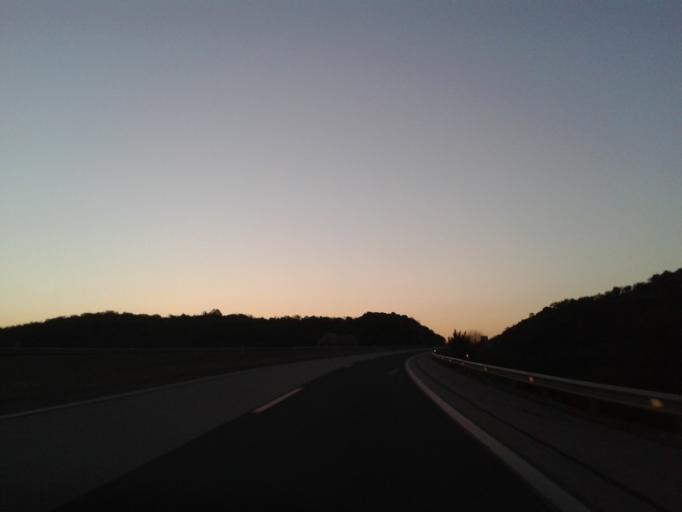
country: PT
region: Faro
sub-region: Loule
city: Boliqueime
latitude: 37.1585
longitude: -8.1816
